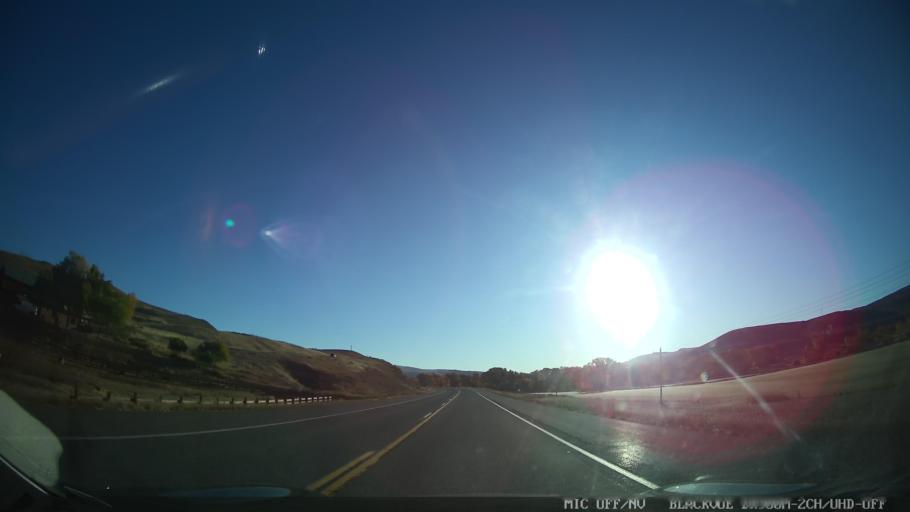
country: US
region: Colorado
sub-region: Grand County
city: Hot Sulphur Springs
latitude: 40.0629
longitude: -106.2428
